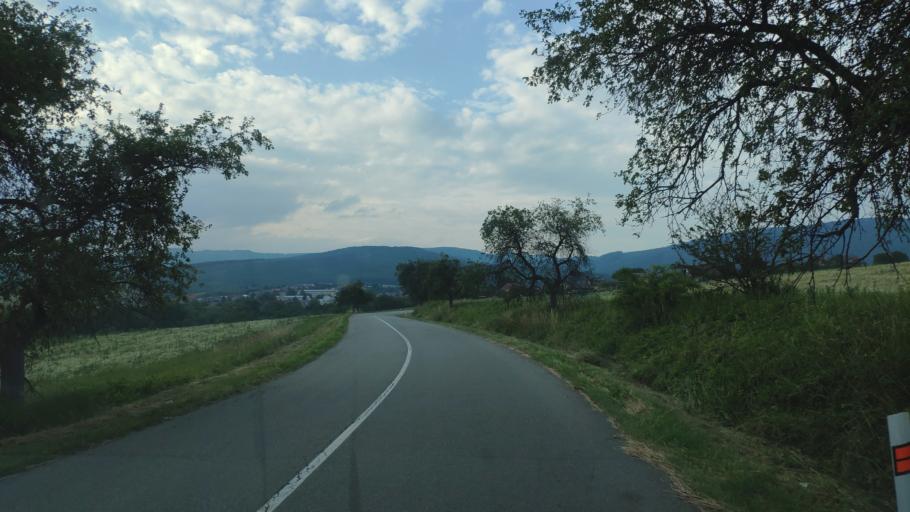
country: SK
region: Kosicky
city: Medzev
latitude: 48.7010
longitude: 20.9743
